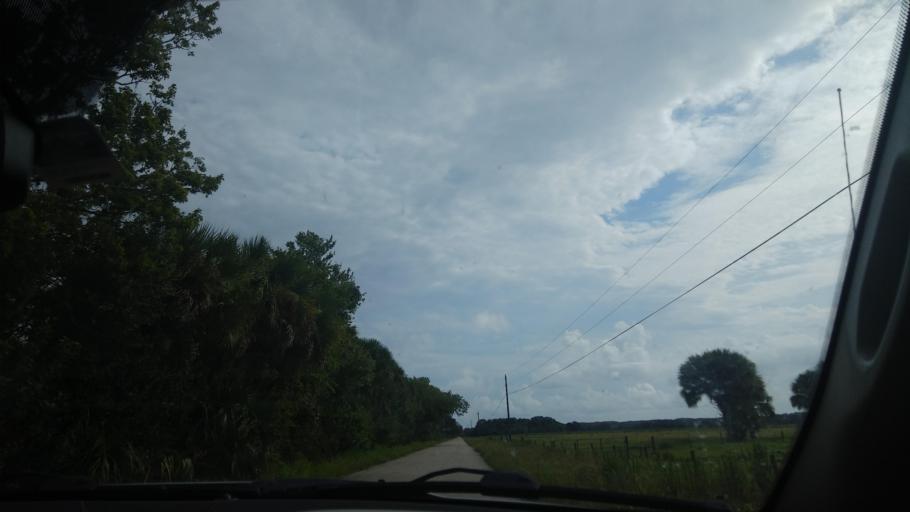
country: US
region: Florida
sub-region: Indian River County
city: Fellsmere
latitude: 27.6972
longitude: -80.7884
